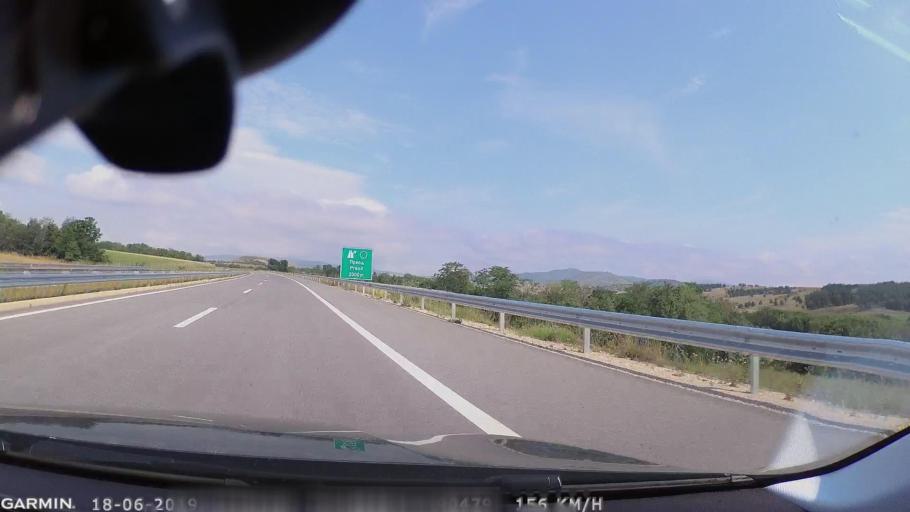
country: MK
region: Sveti Nikole
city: Gorobinci
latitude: 41.9093
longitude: 21.9031
